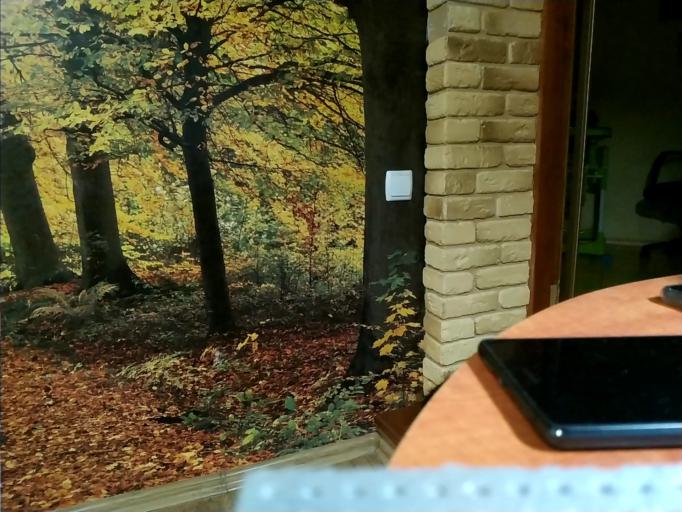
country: RU
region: Tverskaya
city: Zubtsov
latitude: 56.2828
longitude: 34.6900
